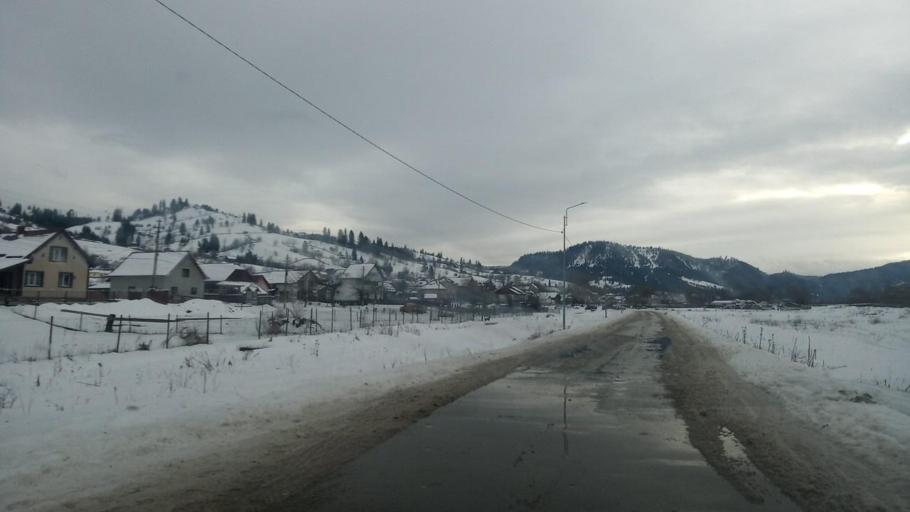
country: RO
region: Suceava
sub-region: Comuna Frasin
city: Plutonita
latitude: 47.5052
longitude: 25.7972
